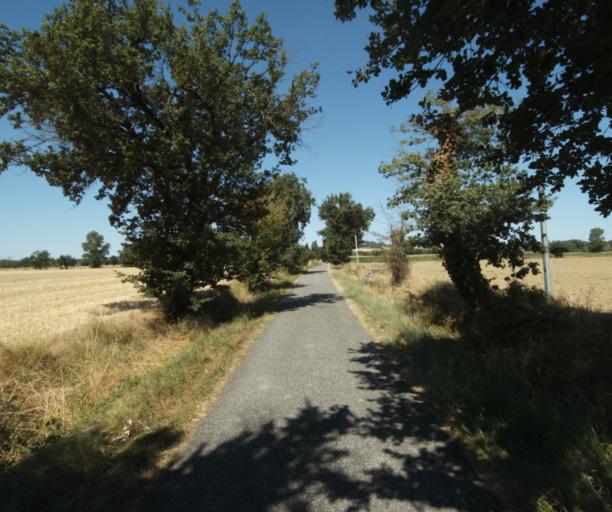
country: FR
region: Midi-Pyrenees
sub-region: Departement de la Haute-Garonne
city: Revel
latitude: 43.4873
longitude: 1.9623
